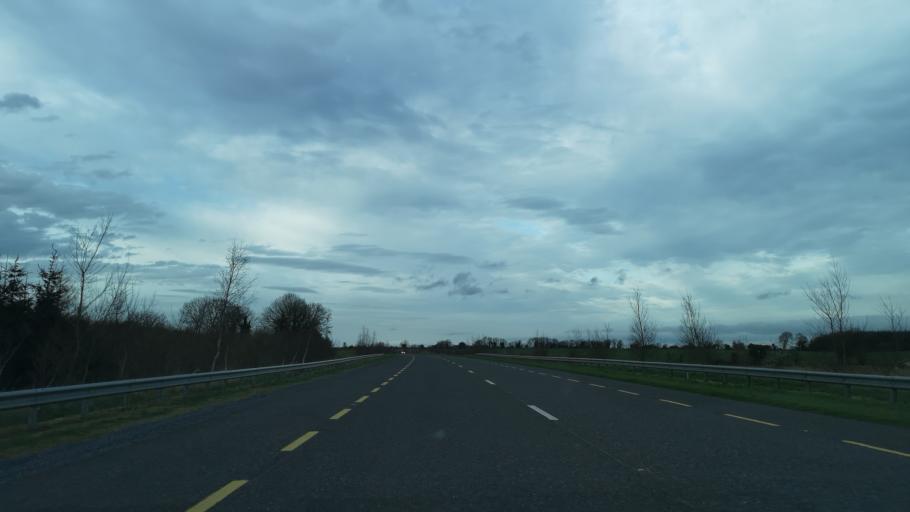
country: IE
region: Connaught
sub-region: County Galway
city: Loughrea
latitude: 53.2431
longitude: -8.5938
